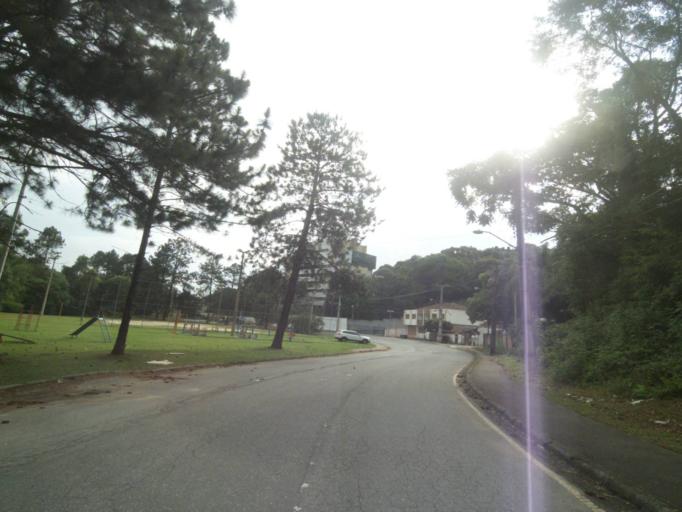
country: BR
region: Parana
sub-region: Curitiba
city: Curitiba
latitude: -25.4094
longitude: -49.3065
